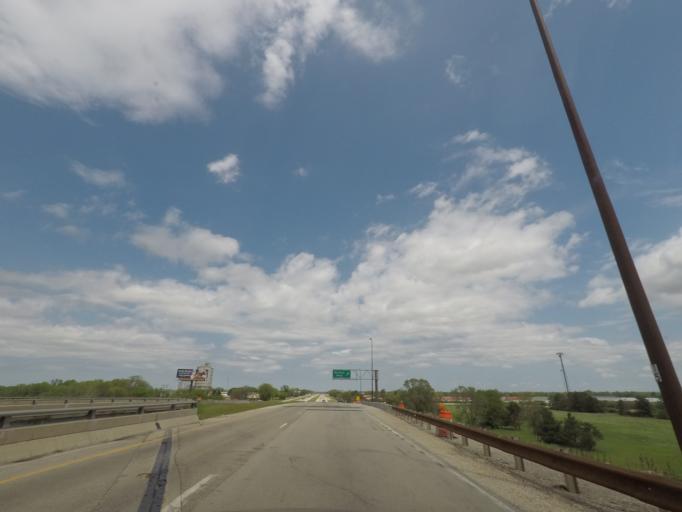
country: US
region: Illinois
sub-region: Winnebago County
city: South Beloit
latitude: 42.4582
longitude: -89.0193
